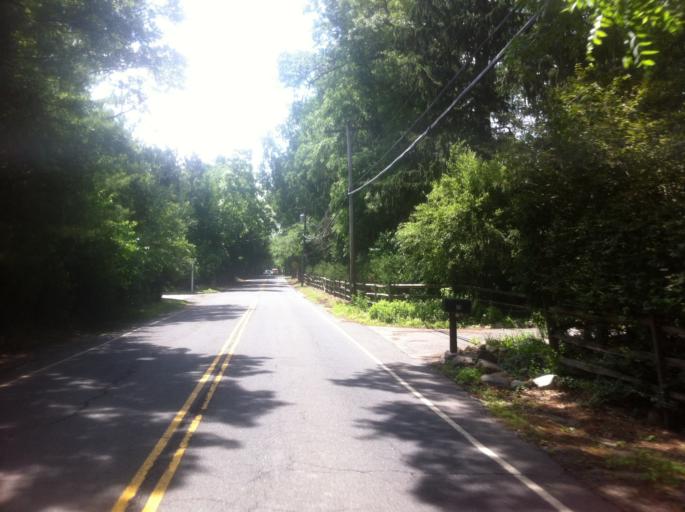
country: US
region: New York
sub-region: Nassau County
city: Old Brookville
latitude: 40.8292
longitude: -73.5914
